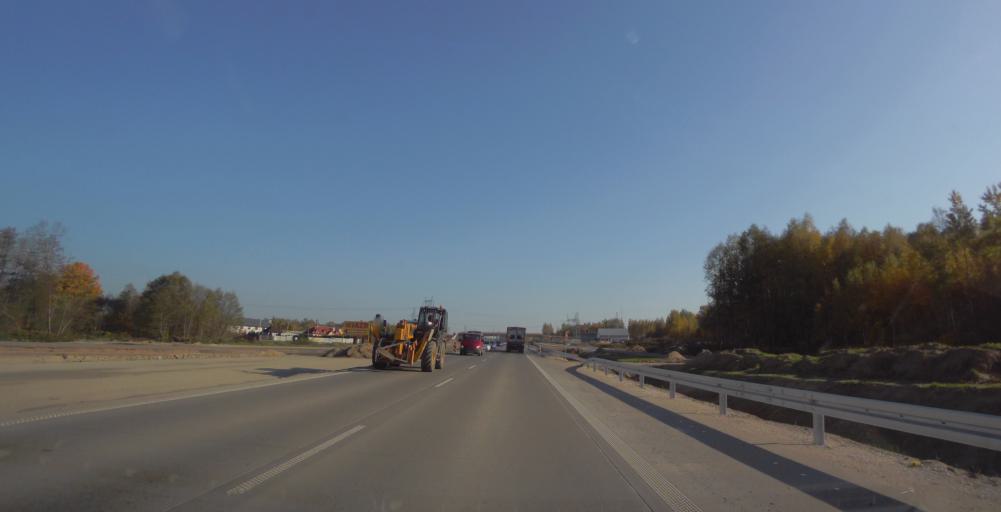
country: PL
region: Masovian Voivodeship
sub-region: Powiat otwocki
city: Celestynow
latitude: 52.1227
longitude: 21.3583
